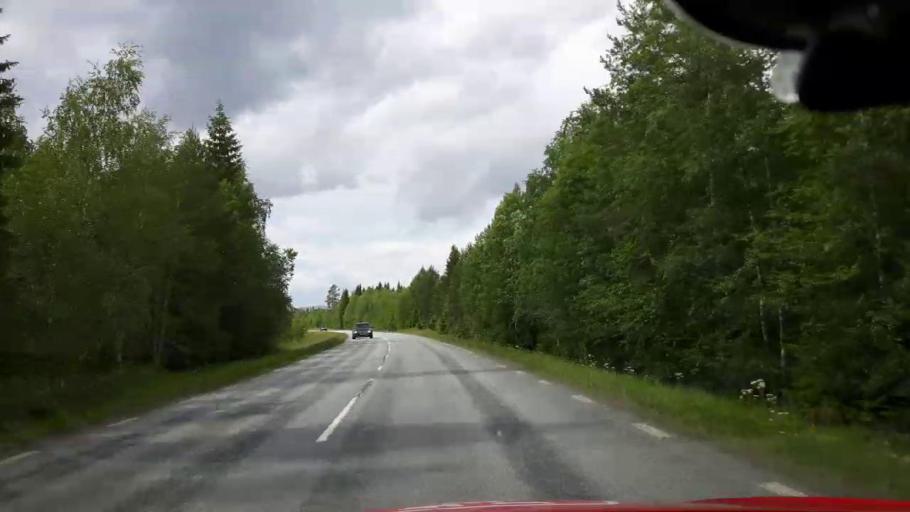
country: SE
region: Jaemtland
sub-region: Krokoms Kommun
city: Krokom
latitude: 63.4032
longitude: 14.3070
